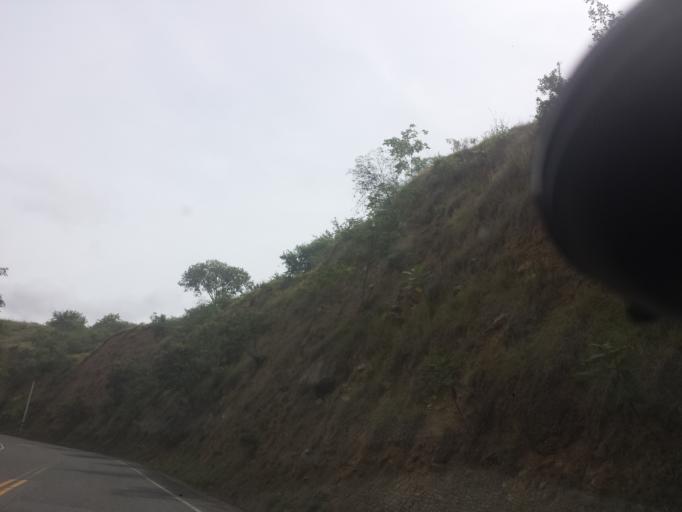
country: CO
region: Antioquia
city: Antioquia
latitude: 6.5648
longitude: -75.8363
